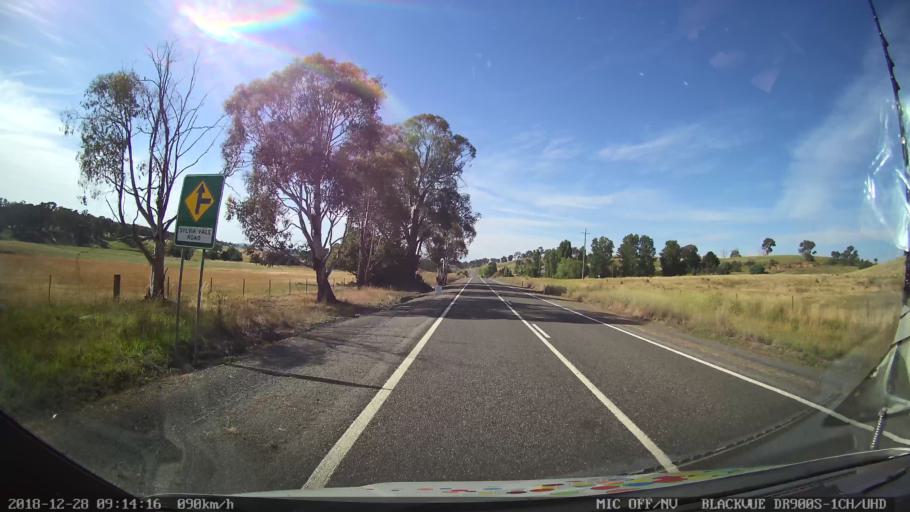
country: AU
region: New South Wales
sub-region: Upper Lachlan Shire
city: Crookwell
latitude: -34.2800
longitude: 149.3455
